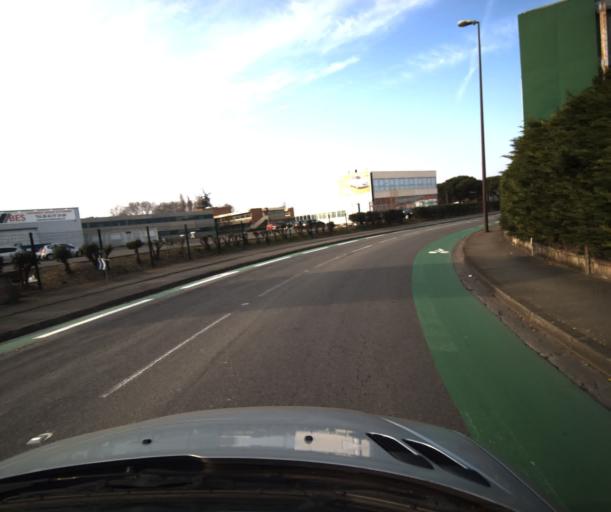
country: FR
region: Midi-Pyrenees
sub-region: Departement de la Haute-Garonne
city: Ramonville-Saint-Agne
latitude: 43.5657
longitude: 1.4893
